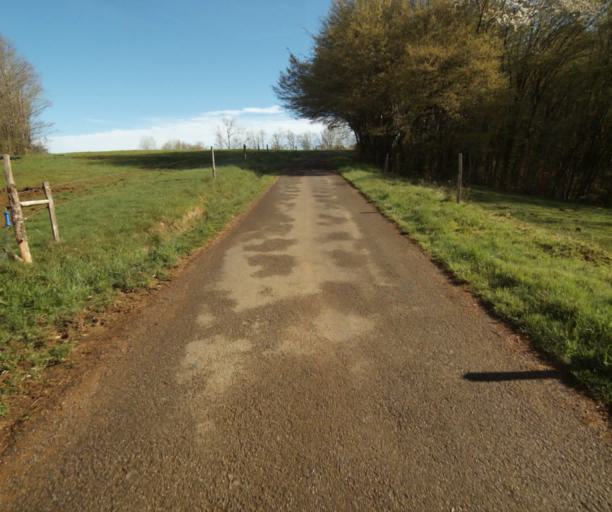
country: FR
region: Limousin
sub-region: Departement de la Correze
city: Laguenne
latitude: 45.2587
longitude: 1.8440
